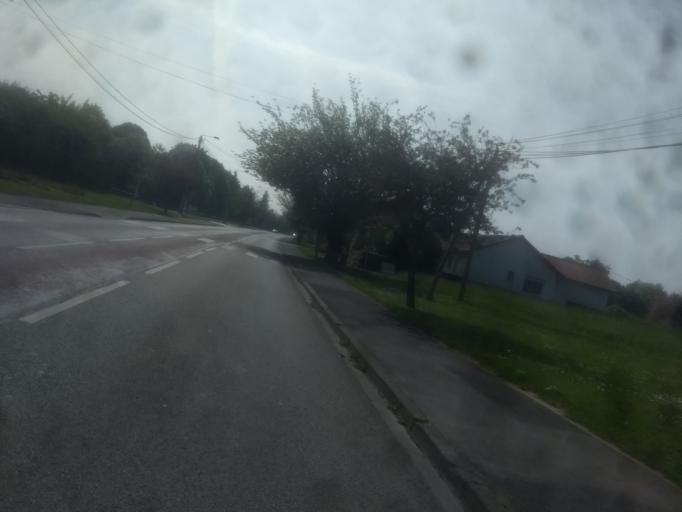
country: FR
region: Nord-Pas-de-Calais
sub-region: Departement du Pas-de-Calais
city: Beaurains
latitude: 50.2607
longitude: 2.7971
